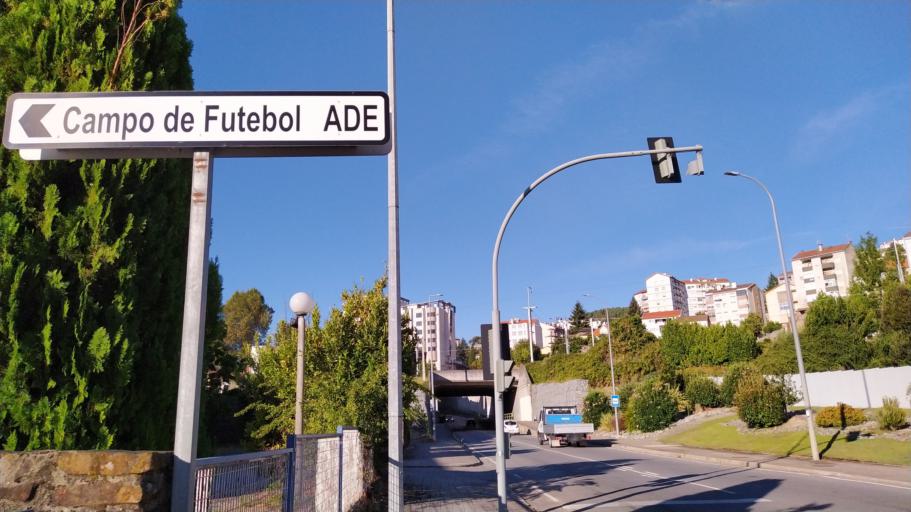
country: PT
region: Castelo Branco
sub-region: Covilha
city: Covilha
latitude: 40.2792
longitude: -7.4954
